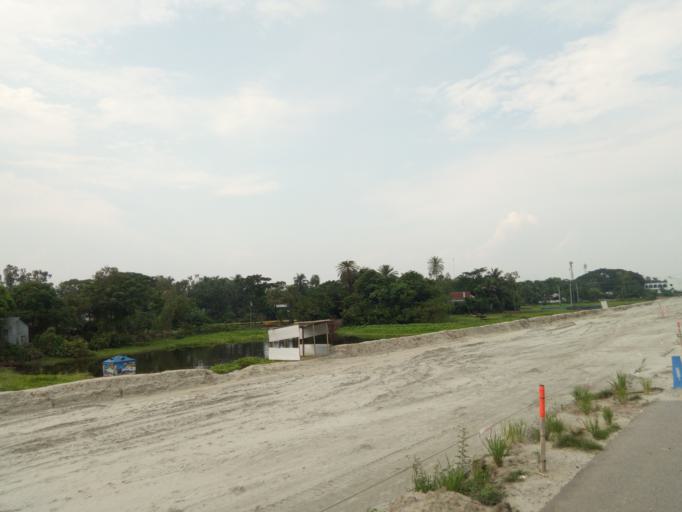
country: BD
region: Dhaka
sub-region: Dhaka
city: Dhaka
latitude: 23.5836
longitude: 90.3078
